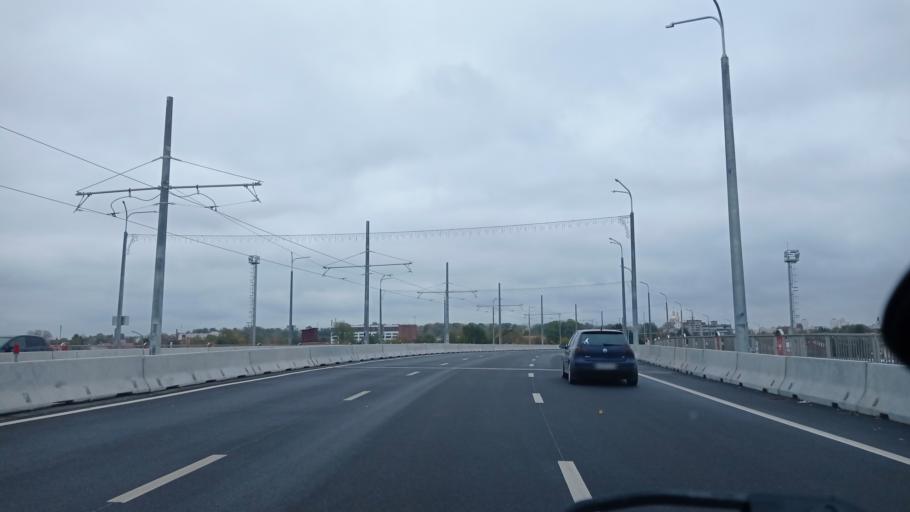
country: BY
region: Vitebsk
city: Vitebsk
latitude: 55.1987
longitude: 30.1843
